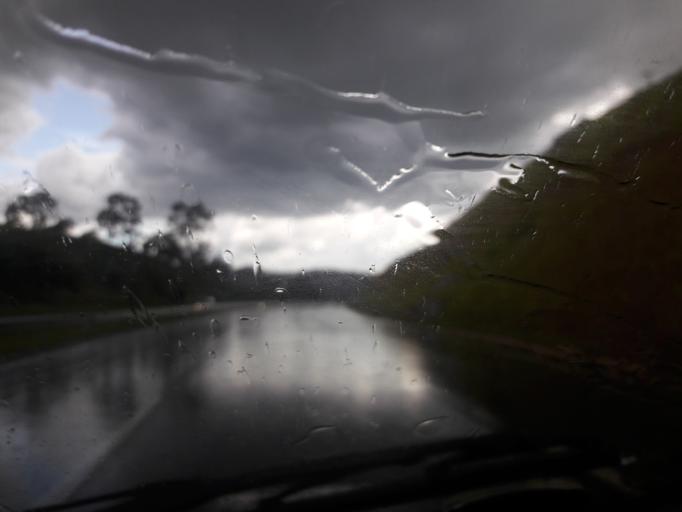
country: BR
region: Sao Paulo
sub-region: Bom Jesus Dos Perdoes
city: Bom Jesus dos Perdoes
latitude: -23.1659
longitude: -46.4066
